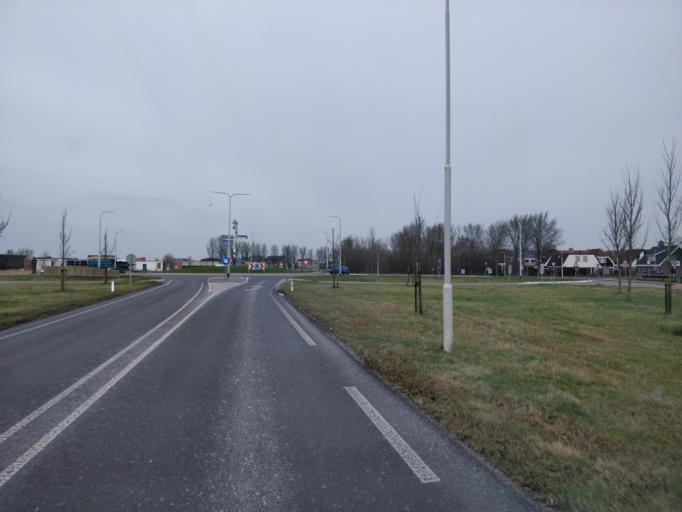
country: NL
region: Friesland
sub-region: Gemeente Leeuwarderadeel
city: Stiens
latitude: 53.2636
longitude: 5.7524
